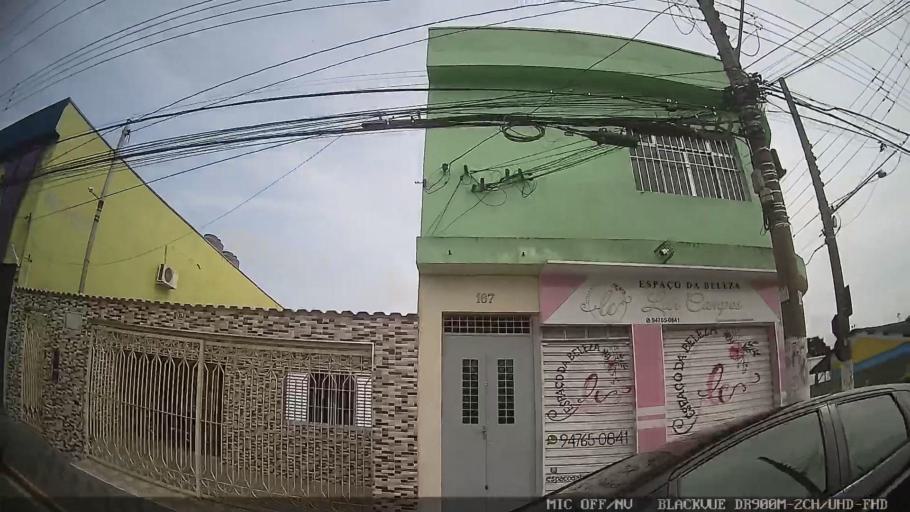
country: BR
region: Sao Paulo
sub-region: Poa
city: Poa
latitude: -23.5207
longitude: -46.3417
